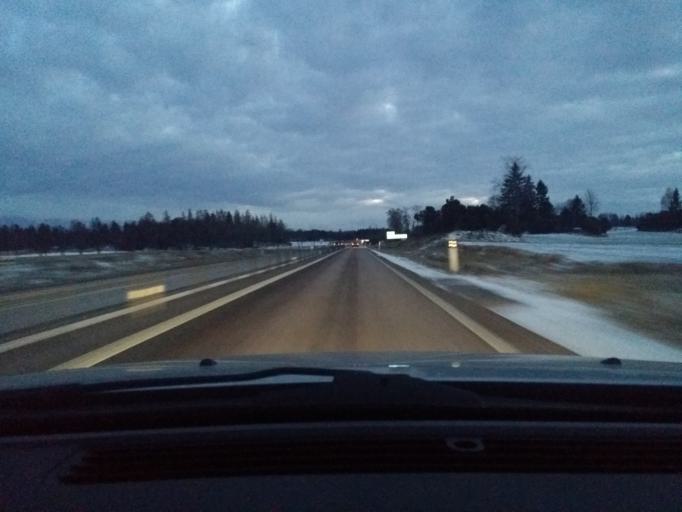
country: SE
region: Uppsala
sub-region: Enkopings Kommun
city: Orsundsbro
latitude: 59.6843
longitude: 17.2774
